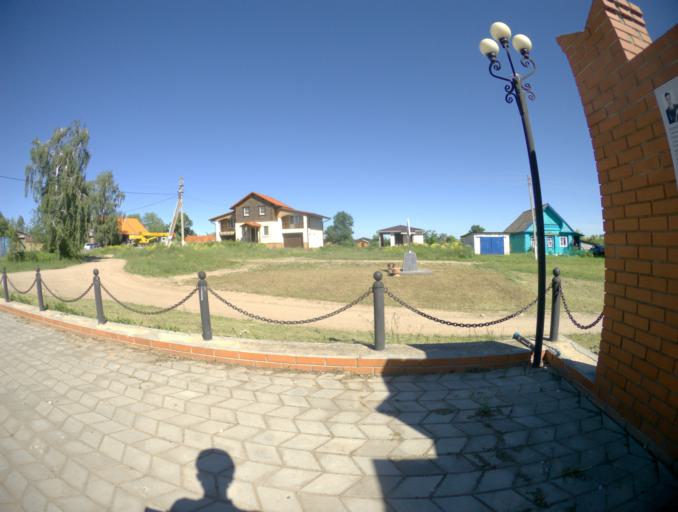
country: RU
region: Vladimir
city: Yur'yev-Pol'skiy
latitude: 56.6074
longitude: 39.8709
